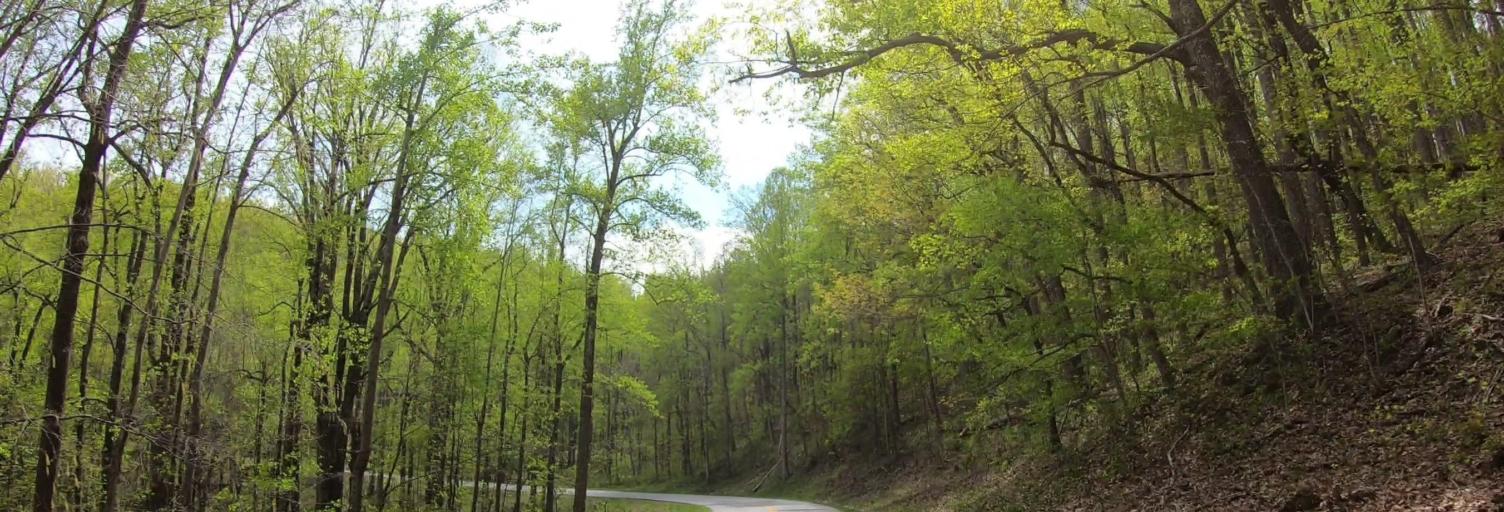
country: US
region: Virginia
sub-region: Botetourt County
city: Buchanan
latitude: 37.4638
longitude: -79.6337
